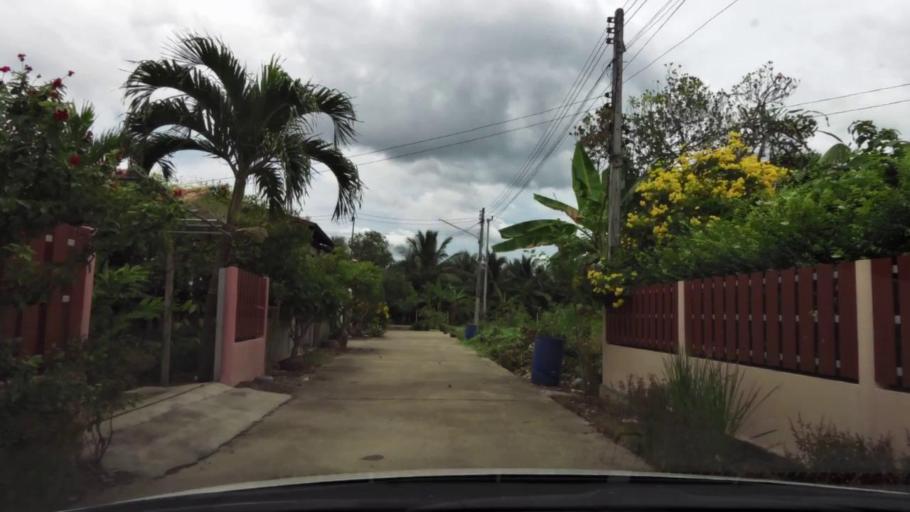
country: TH
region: Samut Sakhon
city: Ban Phaeo
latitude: 13.5730
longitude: 100.0305
